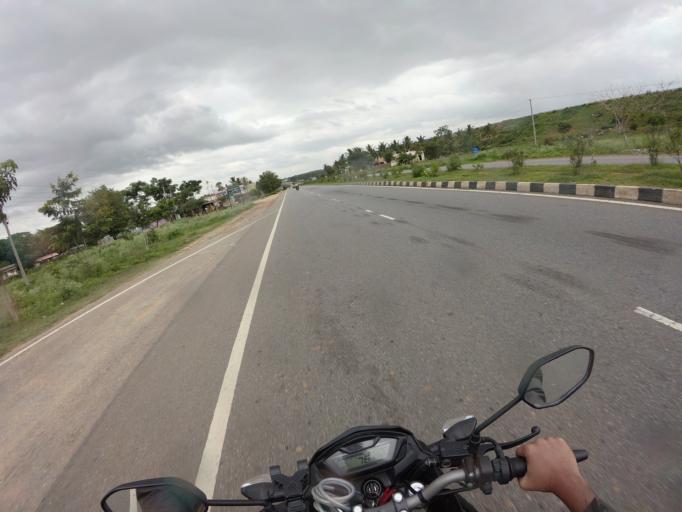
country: IN
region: Karnataka
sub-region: Ramanagara
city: Magadi
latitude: 13.0697
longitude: 77.1830
